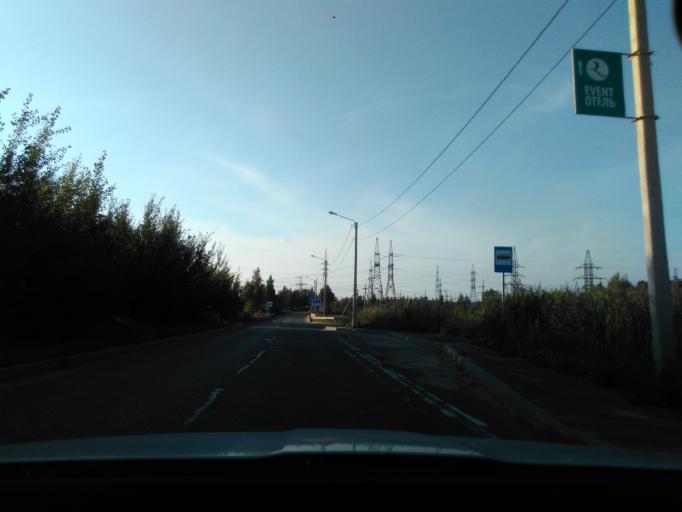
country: RU
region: Tverskaya
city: Konakovo
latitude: 56.7372
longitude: 36.7813
